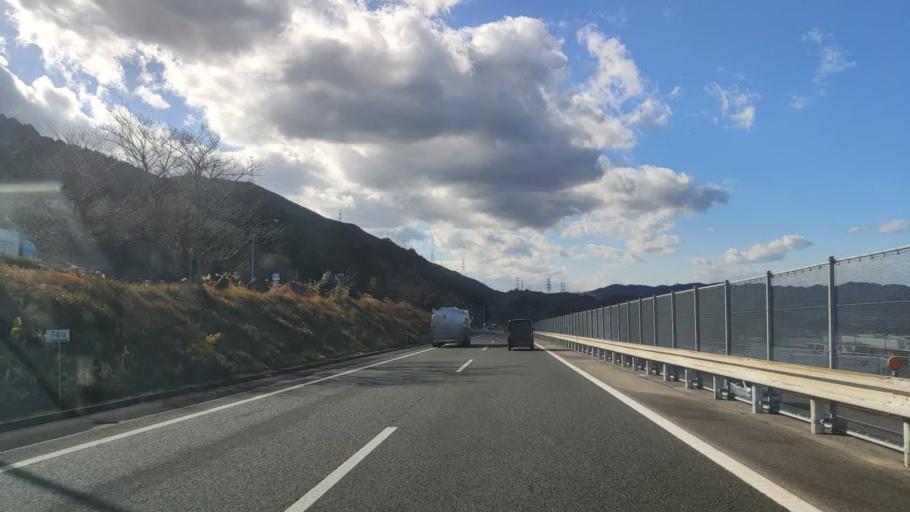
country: JP
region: Ehime
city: Niihama
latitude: 33.9489
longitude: 133.4242
